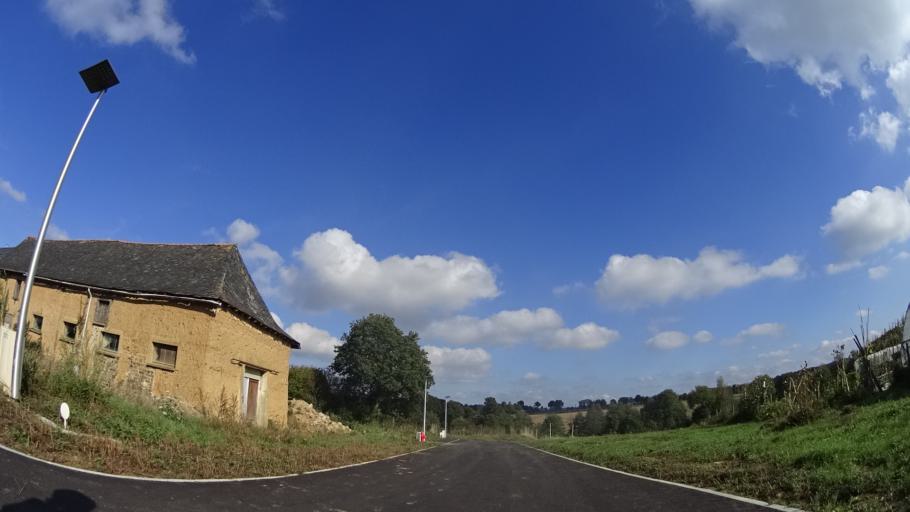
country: FR
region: Brittany
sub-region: Departement d'Ille-et-Vilaine
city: Geveze
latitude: 48.2256
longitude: -1.7918
